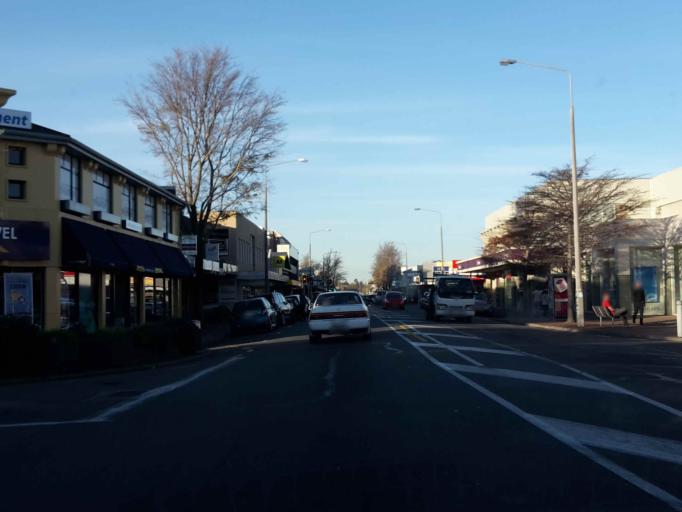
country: NZ
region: Canterbury
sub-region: Christchurch City
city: Christchurch
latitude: -43.5299
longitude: 172.5973
